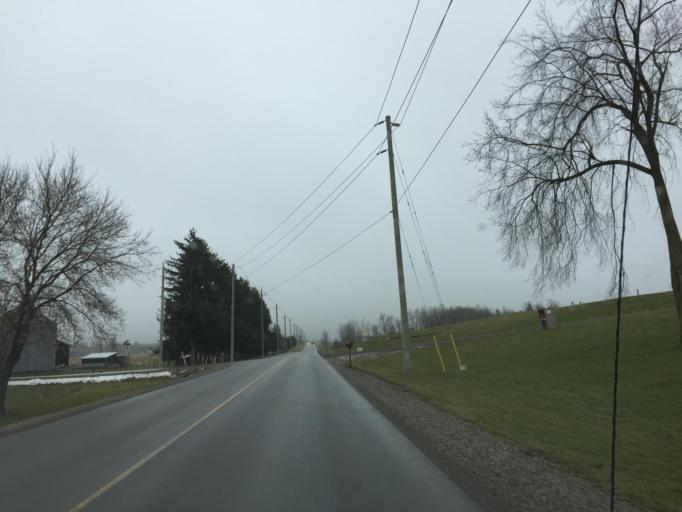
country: CA
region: Ontario
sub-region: Wellington County
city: Guelph
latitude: 43.4782
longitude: -80.3349
